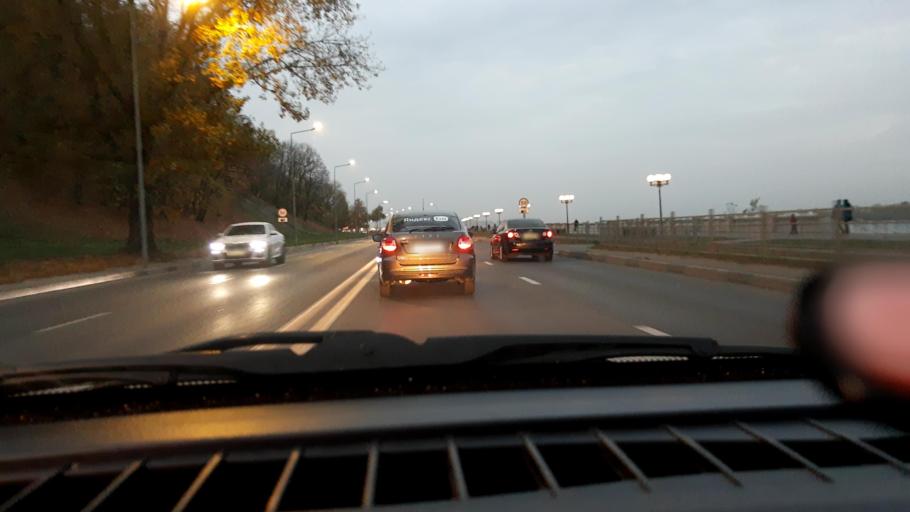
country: RU
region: Nizjnij Novgorod
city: Nizhniy Novgorod
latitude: 56.3320
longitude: 44.0187
